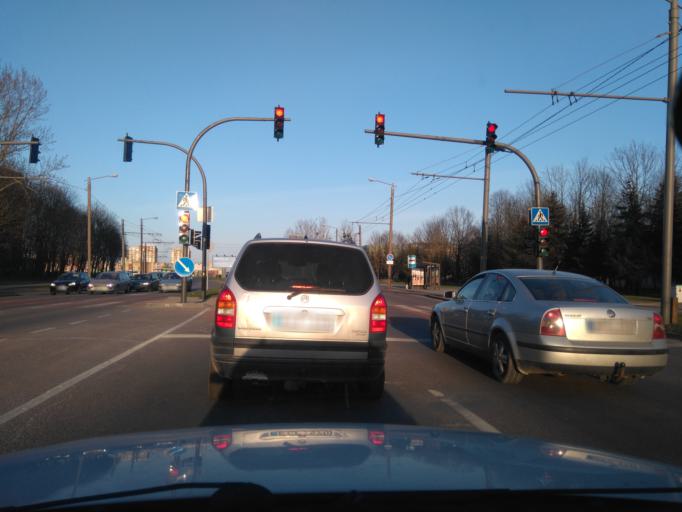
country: LT
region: Kauno apskritis
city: Dainava (Kaunas)
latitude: 54.9118
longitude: 23.9668
